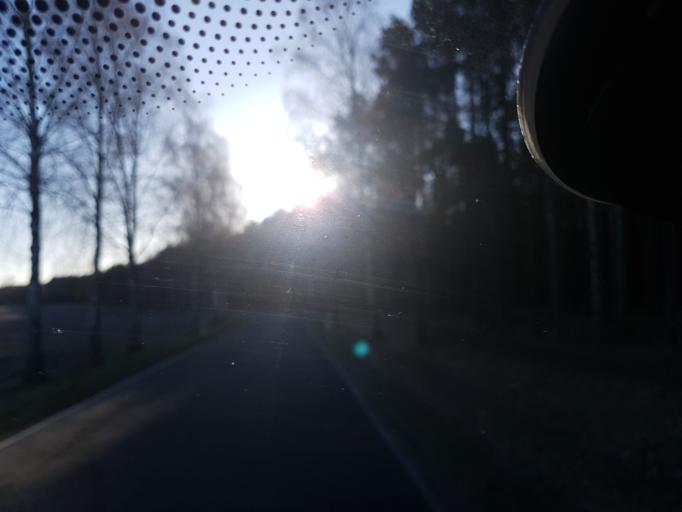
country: DE
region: Brandenburg
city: Jamlitz
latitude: 52.0326
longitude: 14.3549
